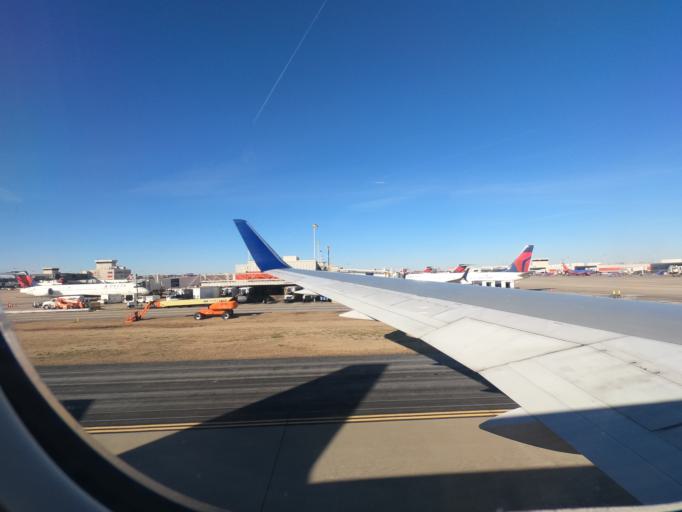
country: US
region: Georgia
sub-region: Fulton County
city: College Park
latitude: 33.6366
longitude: -84.4358
